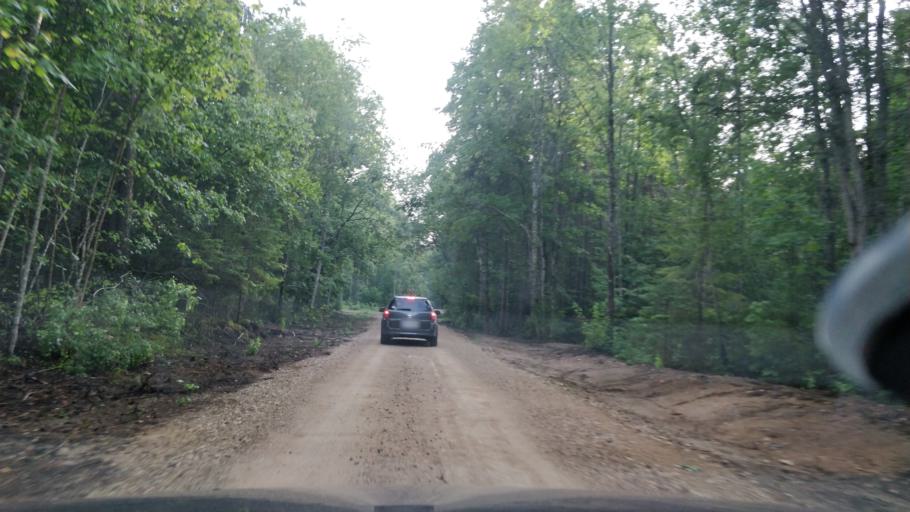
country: LV
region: Incukalns
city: Incukalns
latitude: 57.0994
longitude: 24.7766
